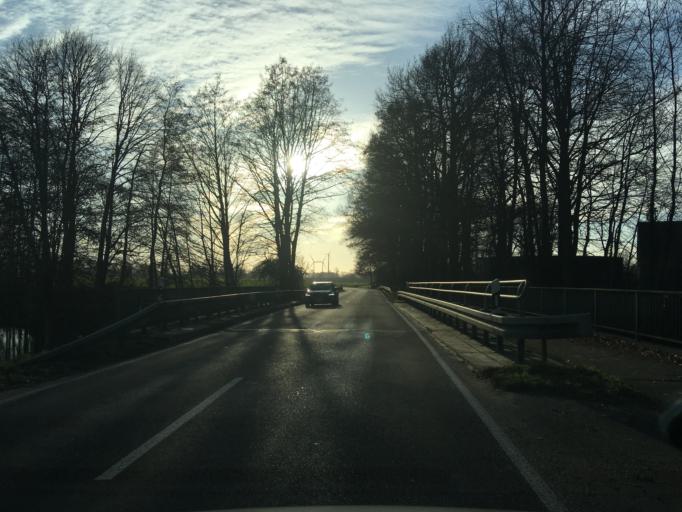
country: DE
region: North Rhine-Westphalia
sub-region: Regierungsbezirk Munster
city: Gescher
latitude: 51.9443
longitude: 7.0484
